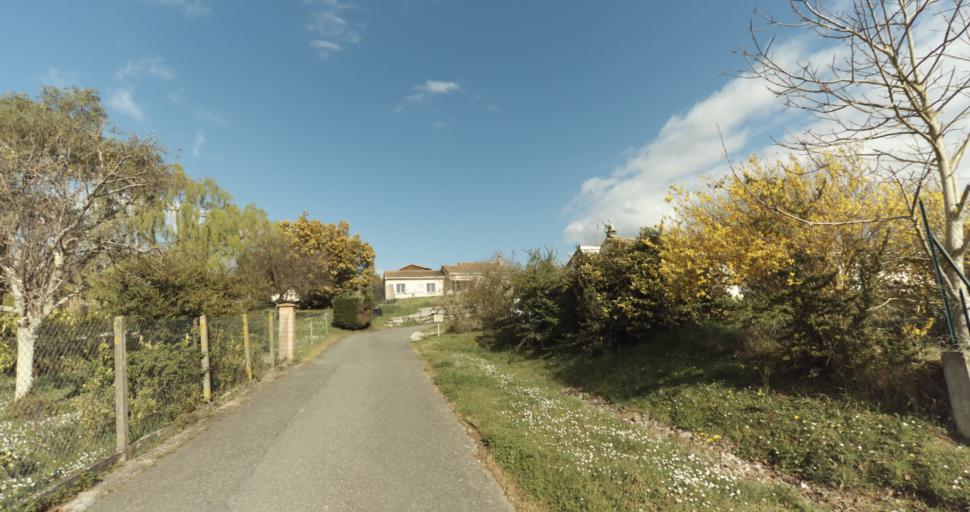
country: FR
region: Midi-Pyrenees
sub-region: Departement de la Haute-Garonne
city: Auterive
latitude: 43.3450
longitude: 1.4888
